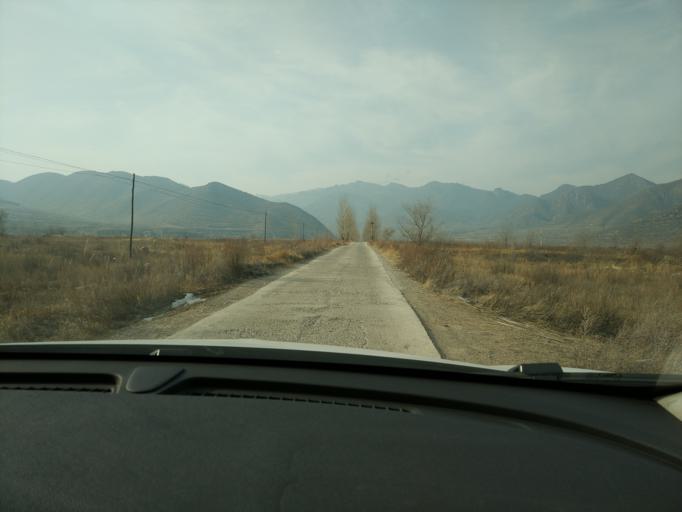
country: CN
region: Hebei
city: Xiwanzi
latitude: 40.8204
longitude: 115.5278
